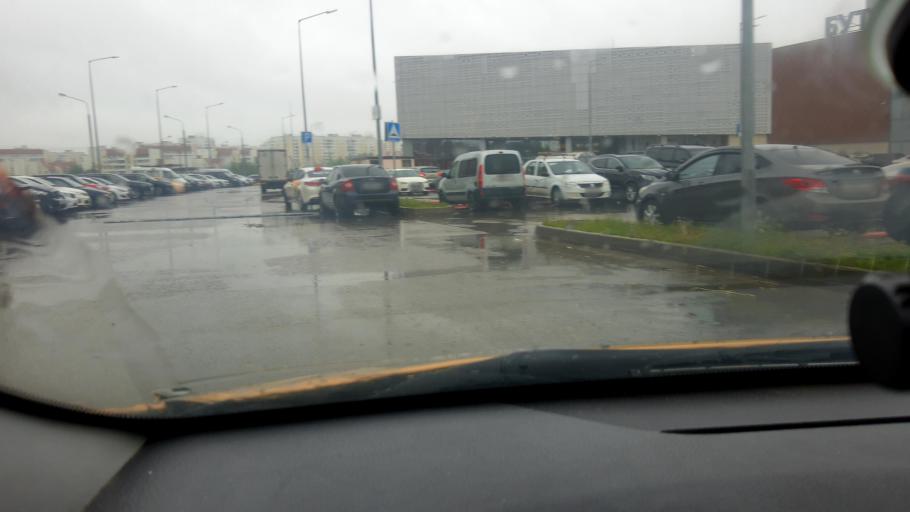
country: RU
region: Moskovskaya
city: Shcherbinka
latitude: 55.5234
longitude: 37.5157
